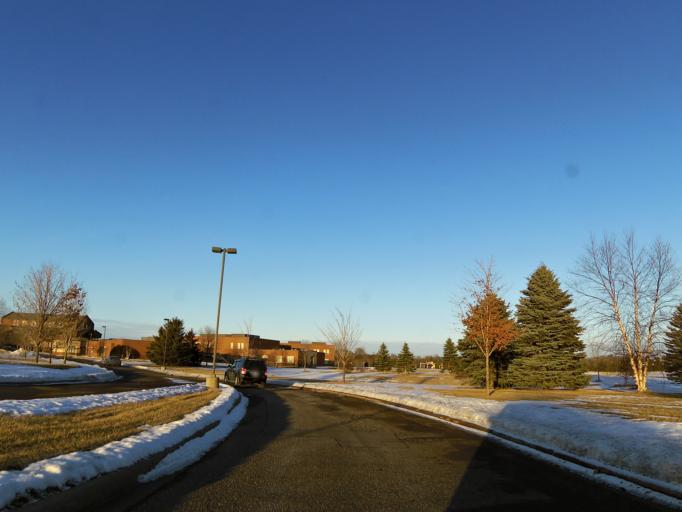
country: US
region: Minnesota
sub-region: Washington County
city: Woodbury
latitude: 44.8873
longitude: -92.9020
